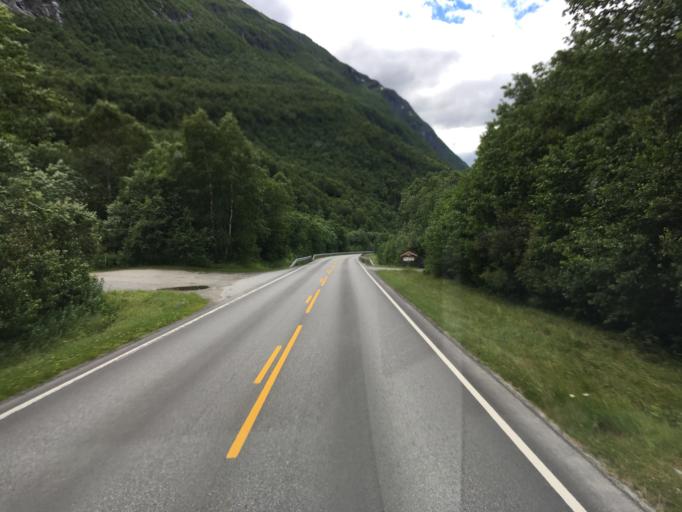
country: NO
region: More og Romsdal
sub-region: Sunndal
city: Sunndalsora
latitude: 62.6336
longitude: 8.8213
